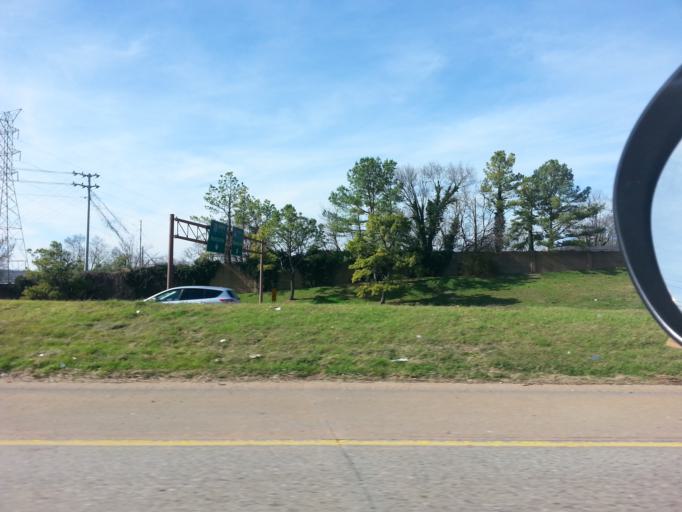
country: US
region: Tennessee
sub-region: Davidson County
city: Oak Hill
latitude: 36.1175
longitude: -86.7690
